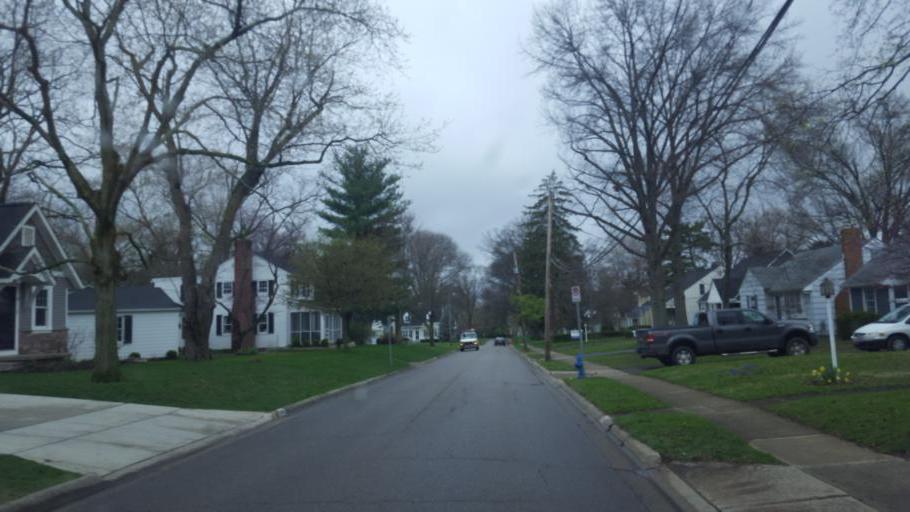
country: US
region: Ohio
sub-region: Franklin County
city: Worthington
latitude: 40.0930
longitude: -83.0186
